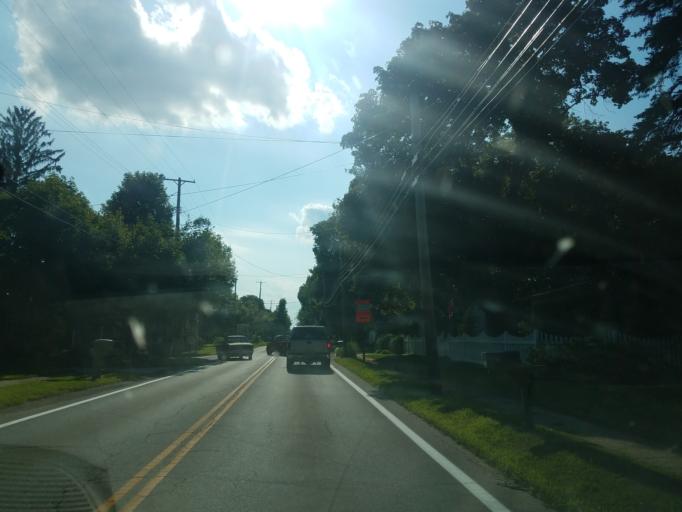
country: US
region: Ohio
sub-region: Stark County
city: Uniontown
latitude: 40.9763
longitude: -81.4132
